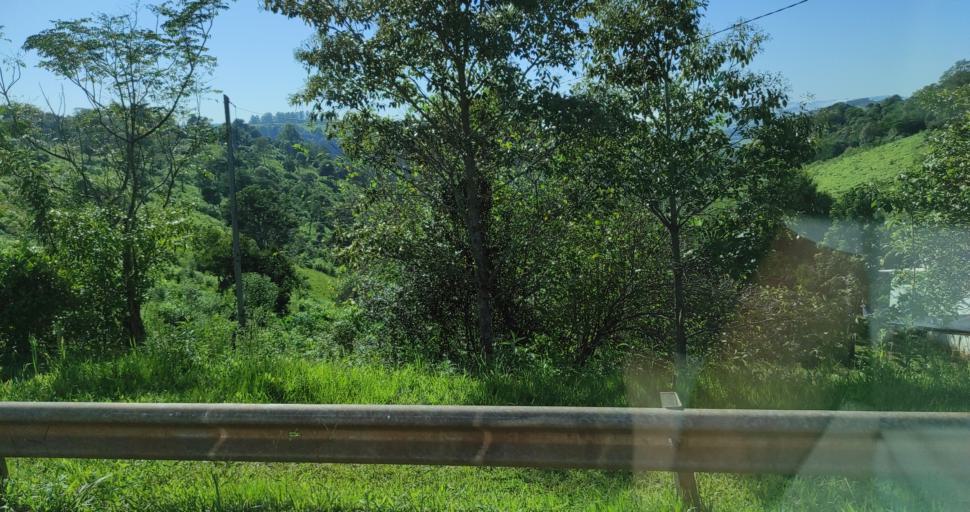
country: AR
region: Misiones
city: El Soberbio
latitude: -27.2440
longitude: -54.1878
